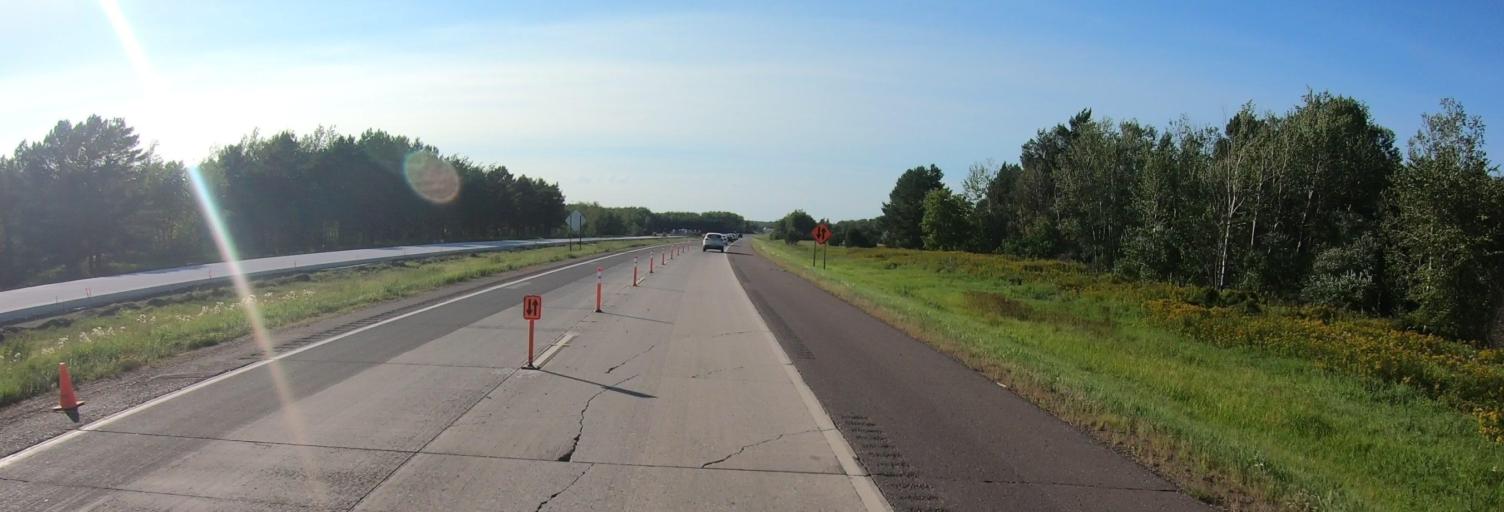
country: US
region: Minnesota
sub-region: Saint Louis County
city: Hermantown
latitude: 46.8690
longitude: -92.3336
